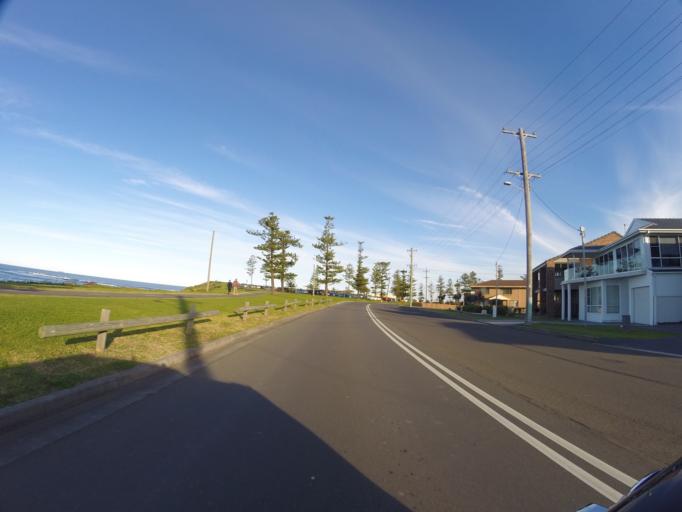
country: AU
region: New South Wales
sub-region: Wollongong
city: Bulli
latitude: -34.3378
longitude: 150.9248
